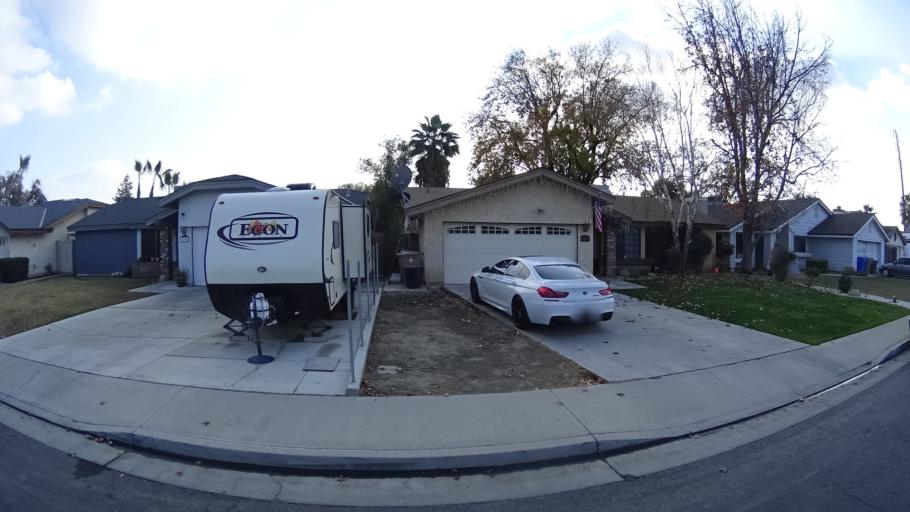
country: US
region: California
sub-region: Kern County
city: Greenacres
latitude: 35.3148
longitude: -119.0953
